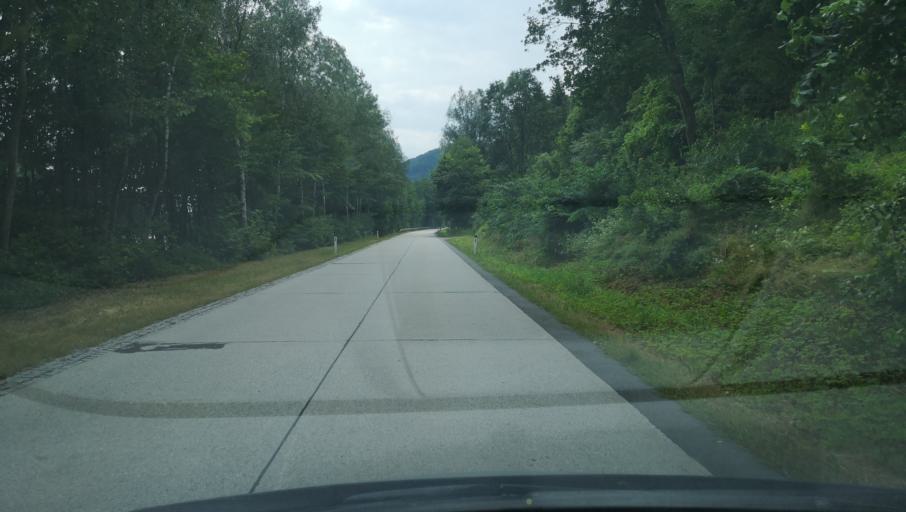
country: AT
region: Lower Austria
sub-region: Politischer Bezirk Melk
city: Nochling
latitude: 48.1935
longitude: 15.0018
